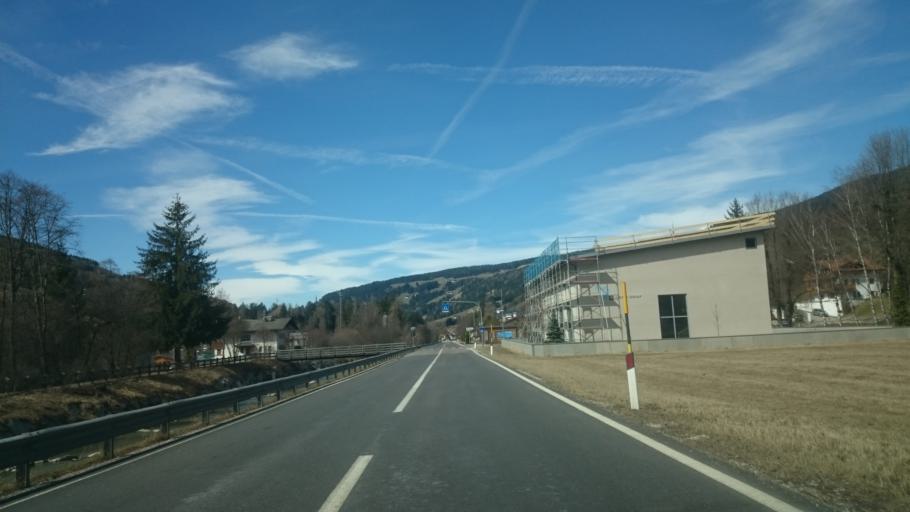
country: IT
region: Trentino-Alto Adige
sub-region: Bolzano
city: Monguelfo
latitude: 46.7523
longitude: 12.1131
